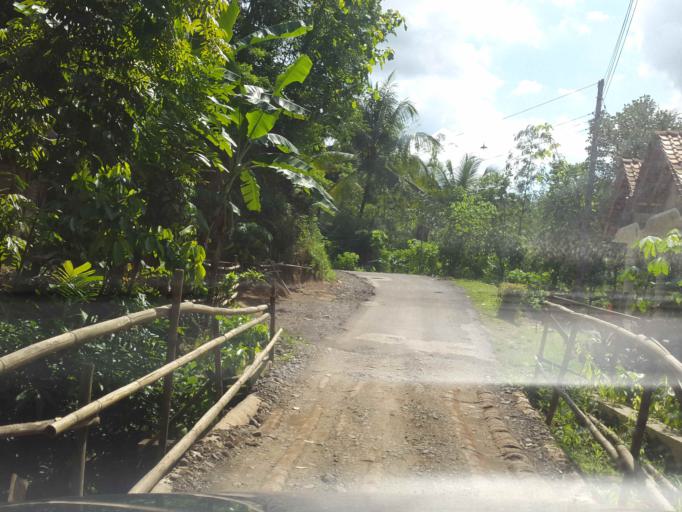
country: ID
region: Central Java
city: Mertoyudan
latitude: -7.6641
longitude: 110.1110
